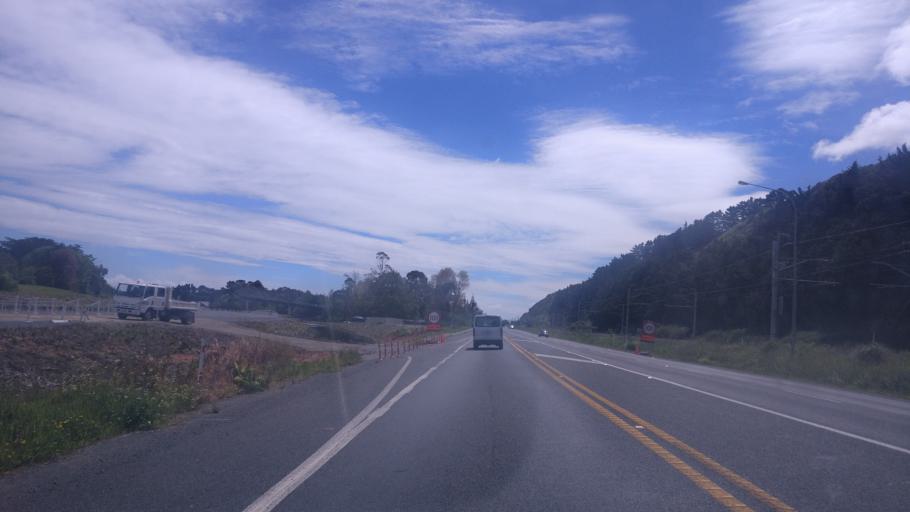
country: NZ
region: Wellington
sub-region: Kapiti Coast District
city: Paraparaumu
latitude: -40.9364
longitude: 174.9948
